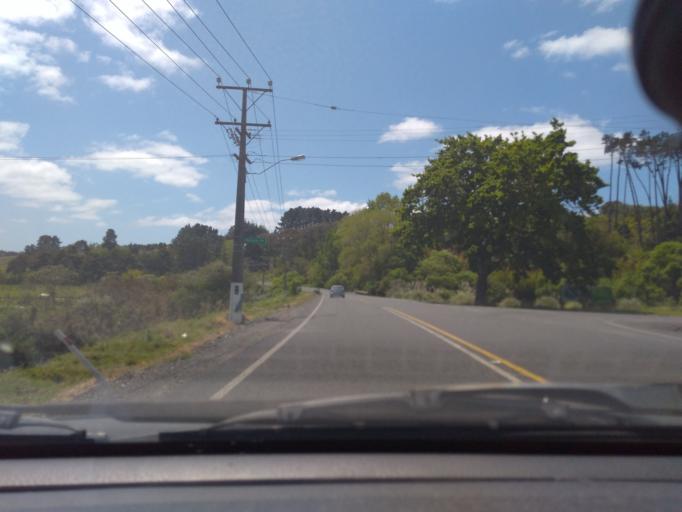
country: NZ
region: Auckland
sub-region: Auckland
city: Pakuranga
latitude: -36.9246
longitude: 174.9973
